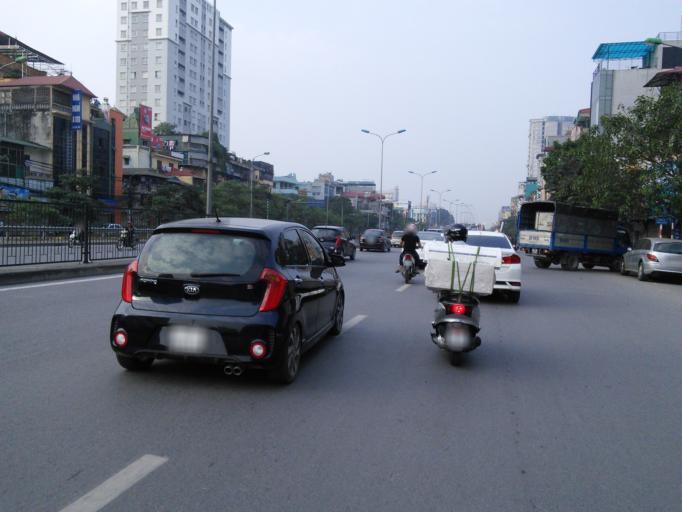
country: VN
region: Ha Noi
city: Hai BaTrung
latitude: 20.9944
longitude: 105.8413
